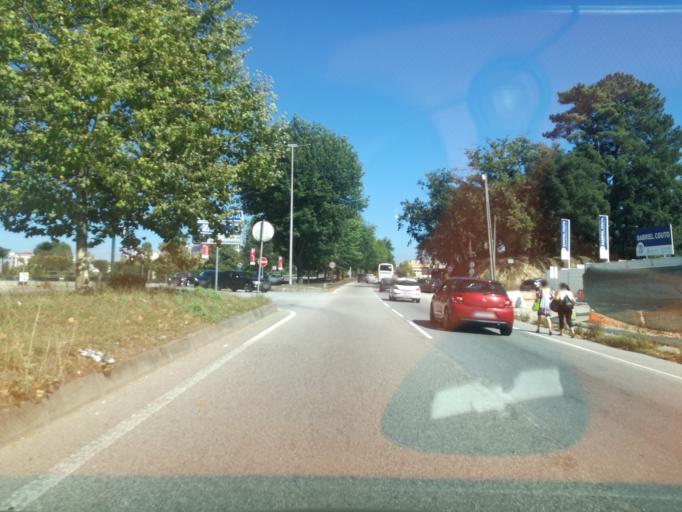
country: PT
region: Porto
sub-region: Maia
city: Pedroucos
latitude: 41.1819
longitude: -8.5962
